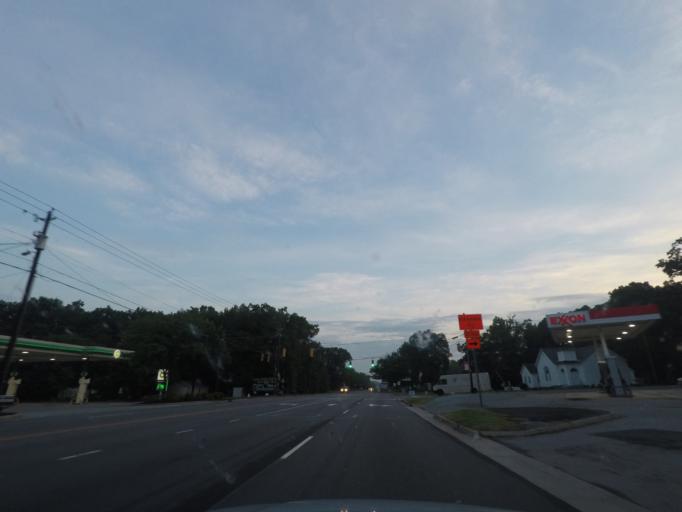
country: US
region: North Carolina
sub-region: Person County
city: Roxboro
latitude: 36.2178
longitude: -78.9259
